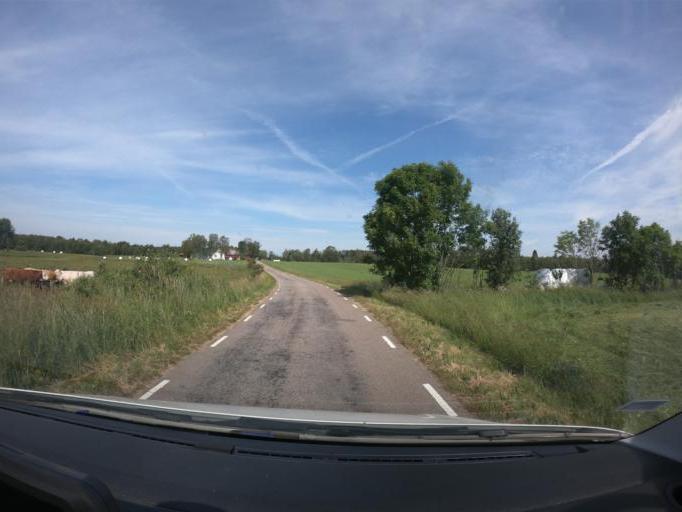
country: SE
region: Skane
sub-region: Bastads Kommun
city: Bastad
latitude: 56.3888
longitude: 12.9576
